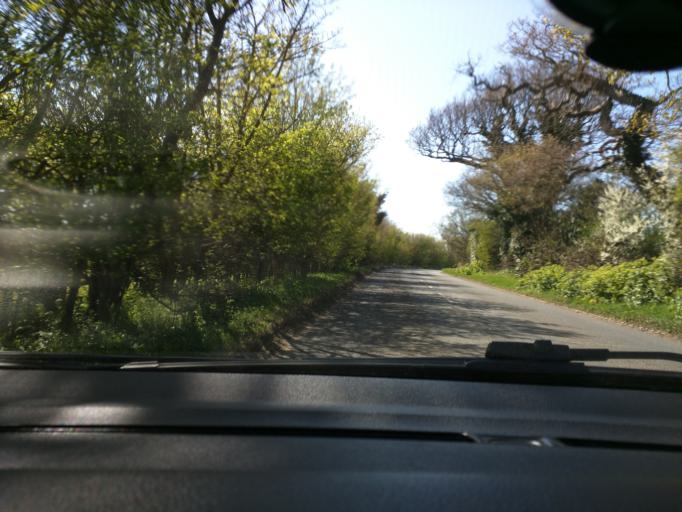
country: GB
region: England
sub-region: Suffolk
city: Leiston
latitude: 52.2175
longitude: 1.5820
